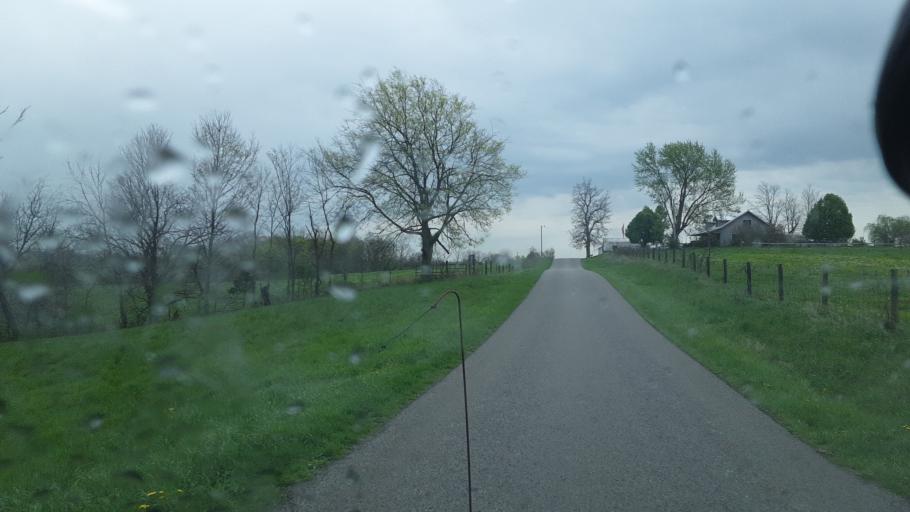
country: US
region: Kentucky
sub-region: Owen County
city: Owenton
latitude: 38.6102
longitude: -84.7813
